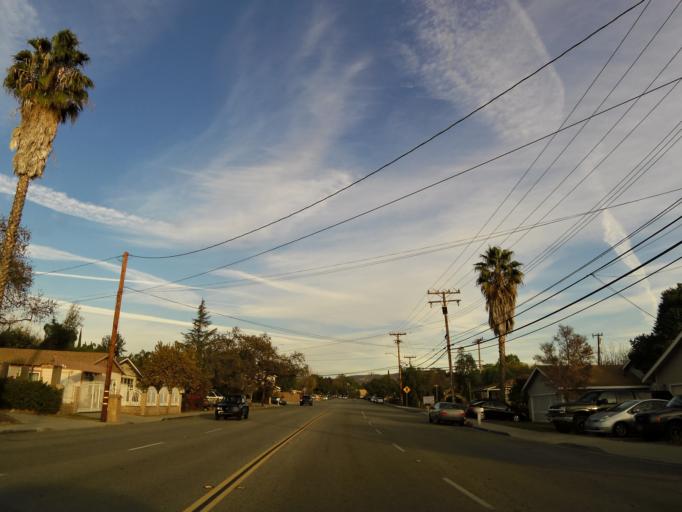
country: US
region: California
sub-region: Ventura County
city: Thousand Oaks
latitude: 34.1814
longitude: -118.8652
